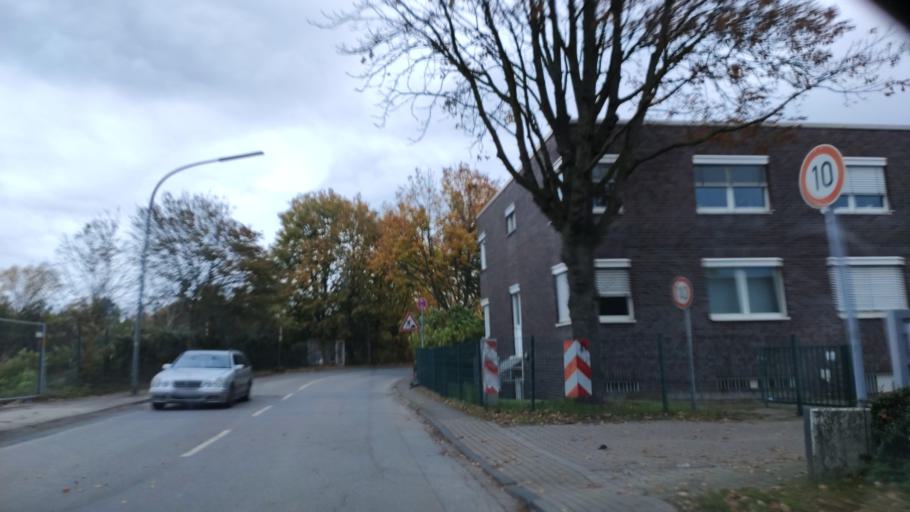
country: DE
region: North Rhine-Westphalia
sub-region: Regierungsbezirk Munster
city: Gelsenkirchen
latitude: 51.5471
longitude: 7.0717
